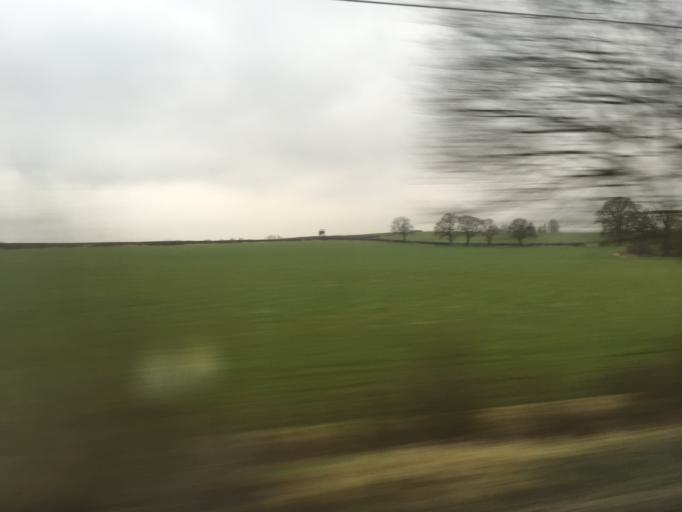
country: GB
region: England
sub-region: Wiltshire
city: Malmesbury
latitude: 51.5417
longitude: -2.1215
